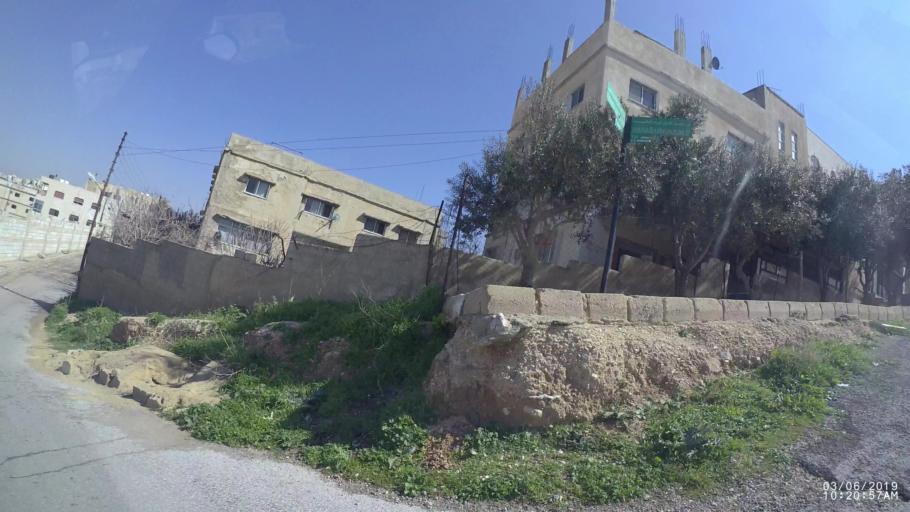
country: JO
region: Amman
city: Amman
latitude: 31.9845
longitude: 35.9792
